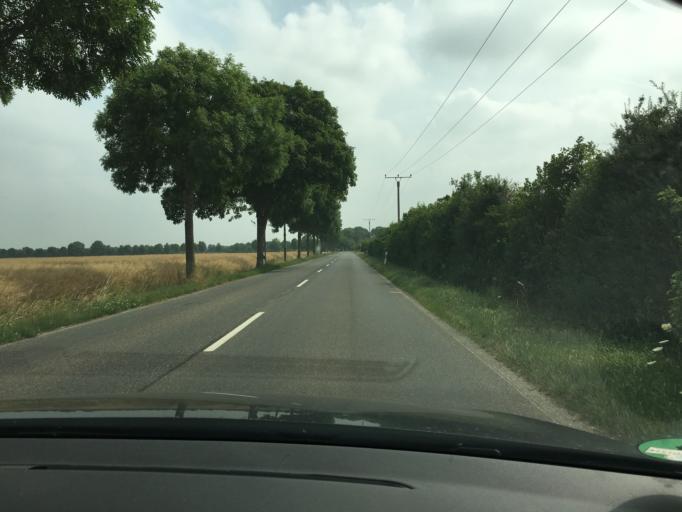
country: DE
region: North Rhine-Westphalia
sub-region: Regierungsbezirk Koln
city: Merzenich
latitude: 50.7979
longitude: 6.5819
